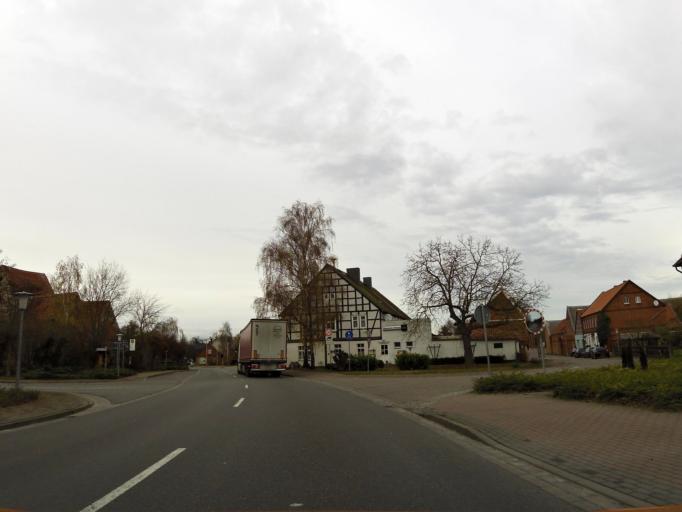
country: DE
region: Saxony-Anhalt
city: Pretzier
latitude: 52.7931
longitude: 11.2331
